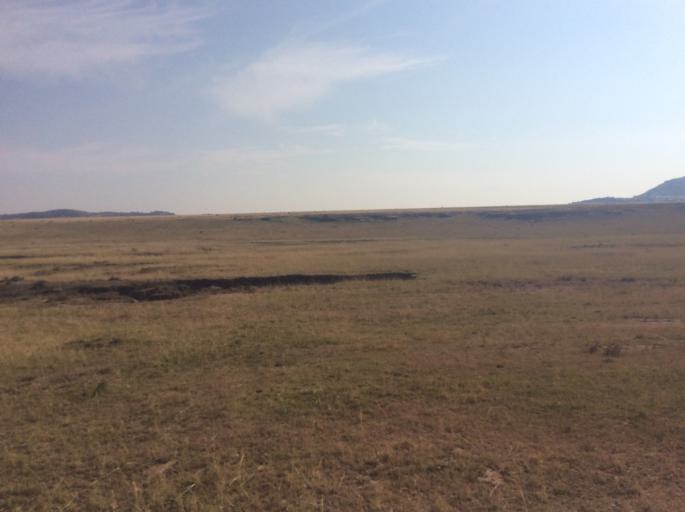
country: LS
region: Mafeteng
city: Mafeteng
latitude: -29.7145
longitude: 27.0060
